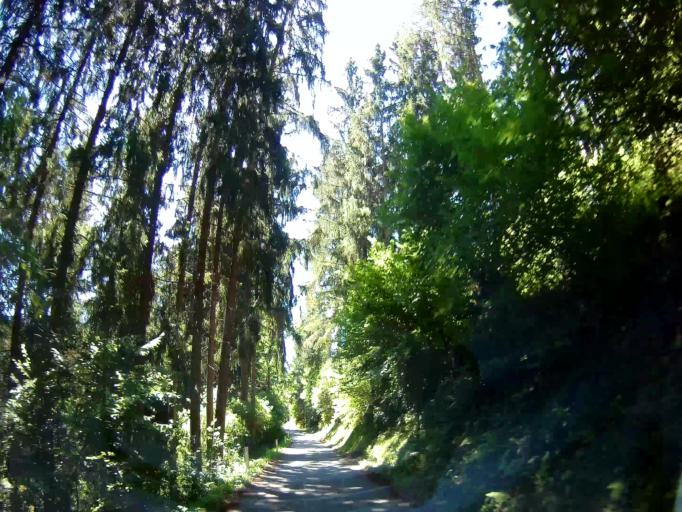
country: AT
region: Carinthia
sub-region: Politischer Bezirk Spittal an der Drau
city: Lendorf
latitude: 46.8221
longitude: 13.4429
